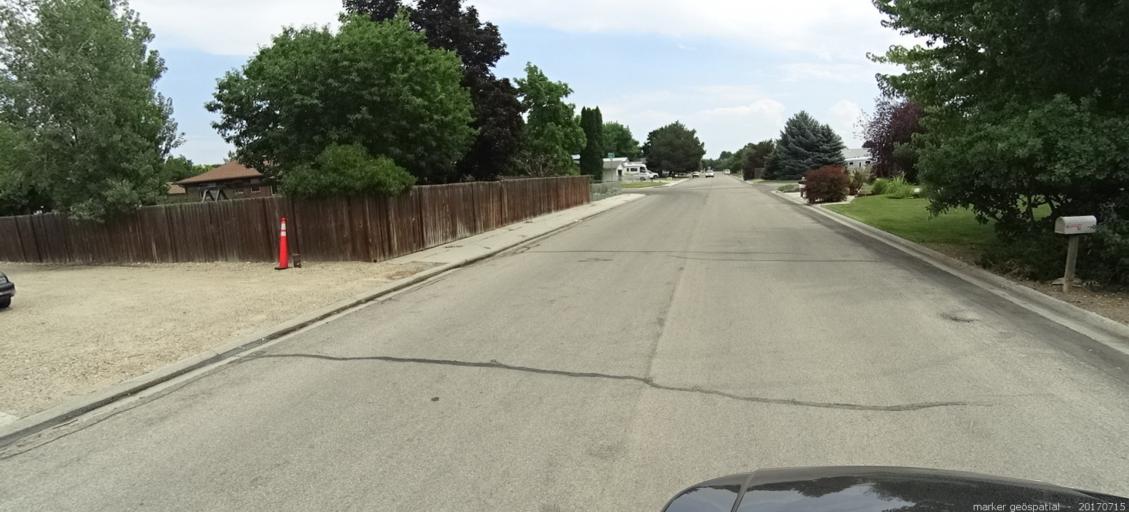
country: US
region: Idaho
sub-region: Ada County
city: Garden City
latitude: 43.5562
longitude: -116.2995
